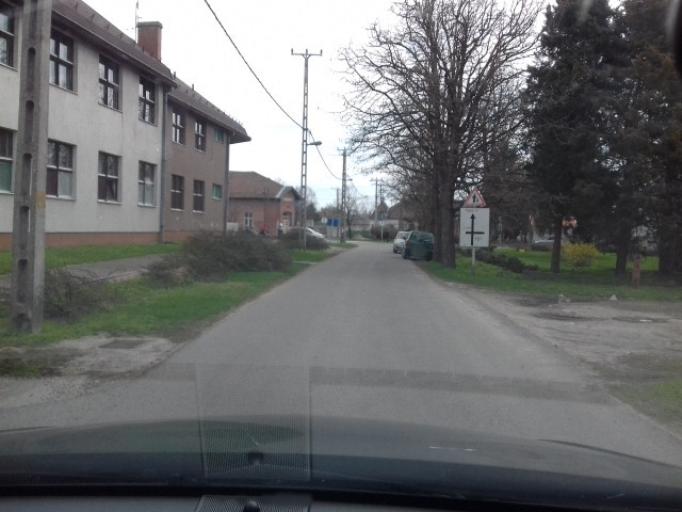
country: HU
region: Bacs-Kiskun
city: Tiszakecske
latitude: 46.8861
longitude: 20.1189
